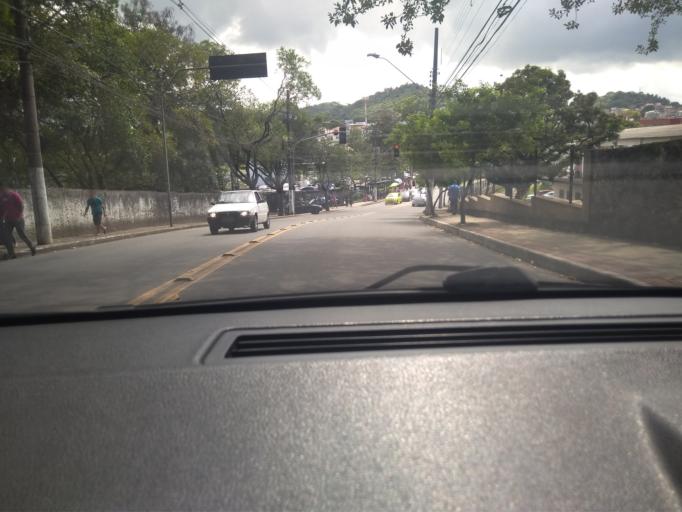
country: BR
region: Espirito Santo
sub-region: Vitoria
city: Vitoria
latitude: -20.2988
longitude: -40.3167
